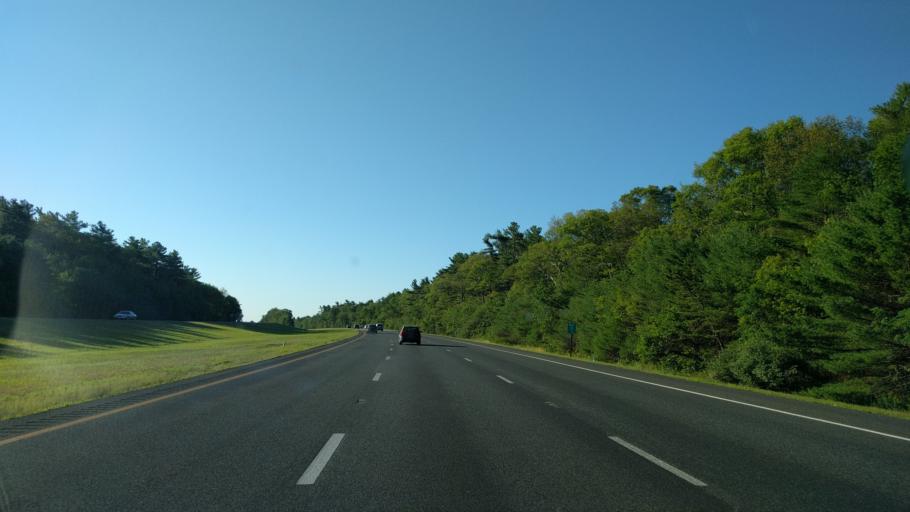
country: US
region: Massachusetts
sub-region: Bristol County
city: Raynham Center
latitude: 41.9400
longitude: -71.0158
